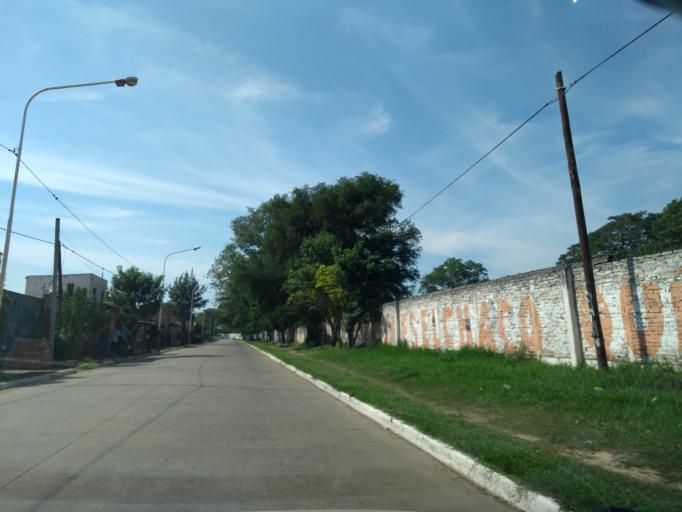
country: AR
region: Chaco
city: Barranqueras
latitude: -27.4644
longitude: -58.9554
